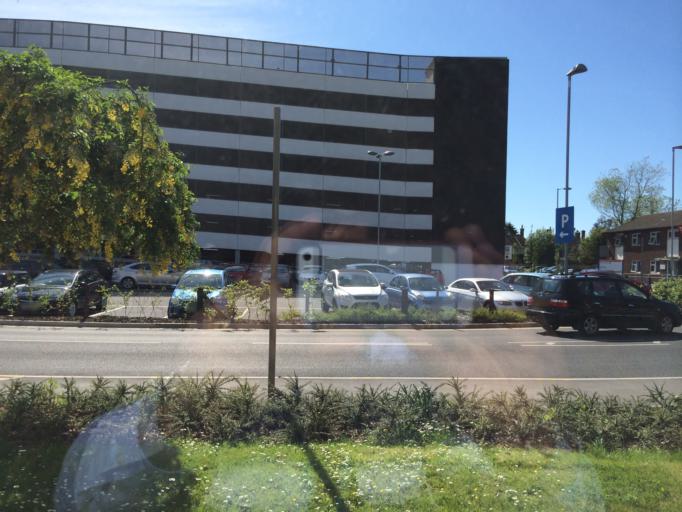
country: GB
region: England
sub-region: Lancashire
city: Great Marton
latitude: 53.8214
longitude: -3.0120
